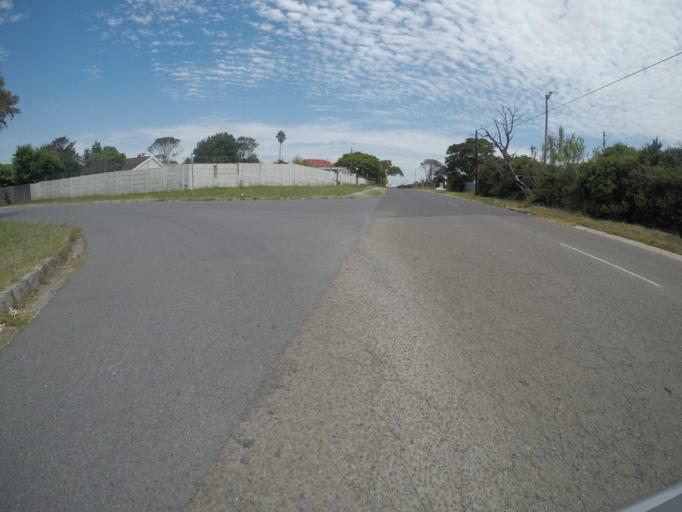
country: ZA
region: Eastern Cape
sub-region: Buffalo City Metropolitan Municipality
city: East London
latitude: -32.9835
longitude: 27.8600
